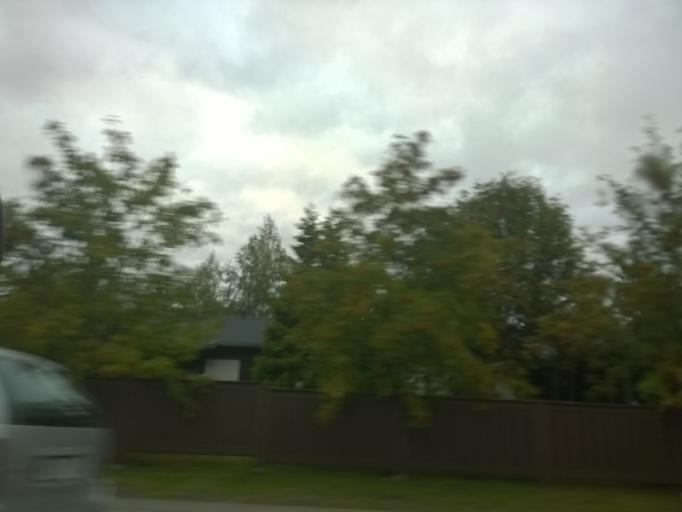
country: FI
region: Pirkanmaa
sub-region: Tampere
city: Tampere
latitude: 61.4569
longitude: 23.8392
